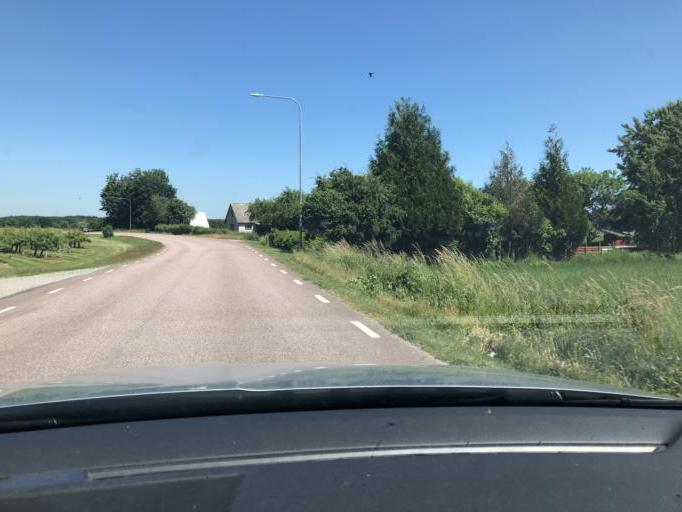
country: SE
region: Blekinge
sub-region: Olofstroms Kommun
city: Jamshog
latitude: 56.1739
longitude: 14.6082
